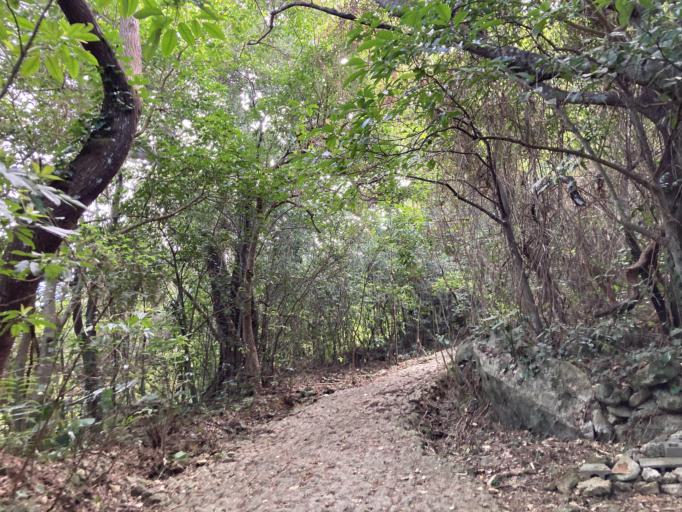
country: JP
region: Okinawa
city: Nago
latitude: 26.6894
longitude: 127.9273
